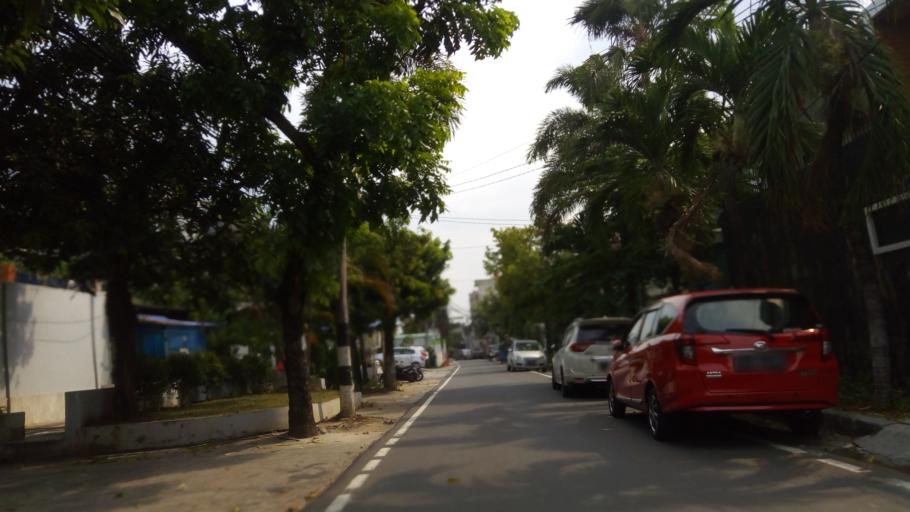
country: ID
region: Jakarta Raya
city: Jakarta
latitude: -6.1545
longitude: 106.8342
